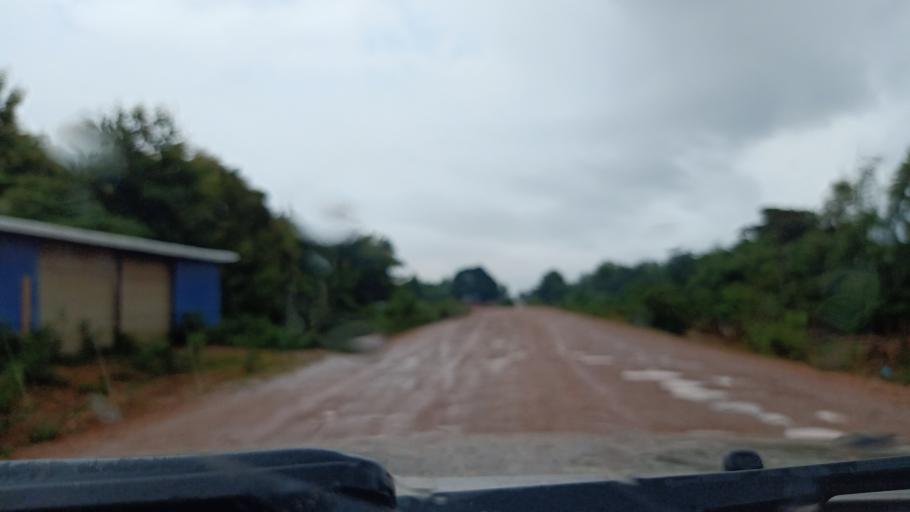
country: LA
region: Attapu
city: Attapu
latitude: 14.7113
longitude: 106.6600
